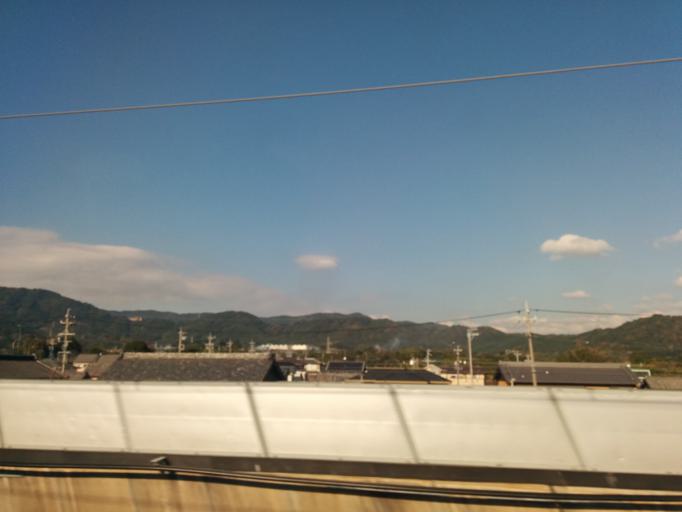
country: JP
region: Aichi
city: Gamagori
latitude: 34.8145
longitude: 137.2928
